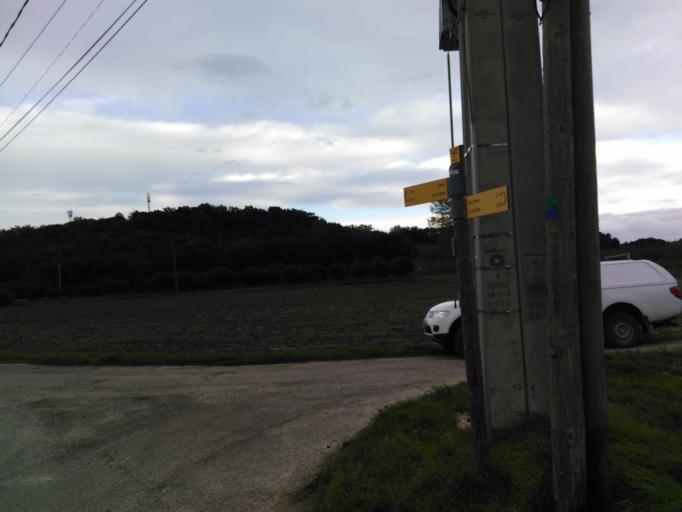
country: FR
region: Provence-Alpes-Cote d'Azur
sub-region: Departement du Vaucluse
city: Grillon
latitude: 44.4086
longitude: 4.9382
